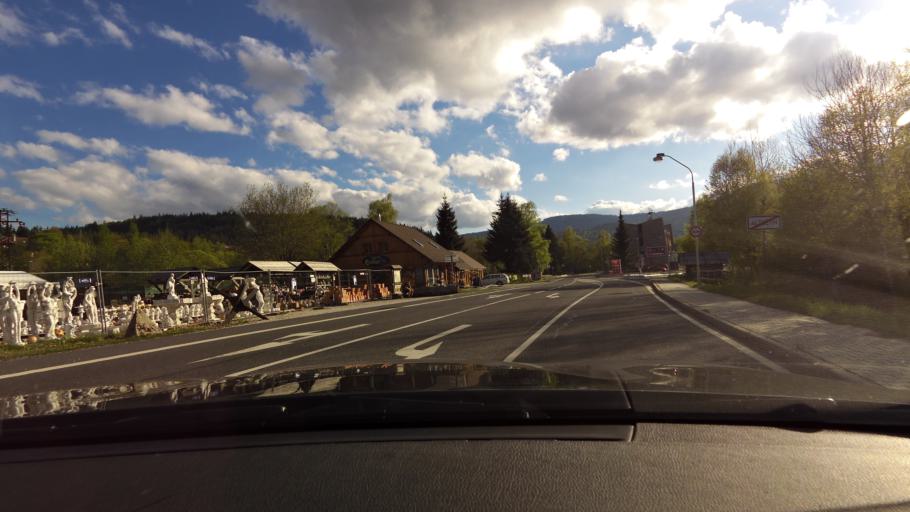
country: DE
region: Bavaria
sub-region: Lower Bavaria
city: Bayerisch Eisenstein
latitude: 49.1242
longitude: 13.2092
